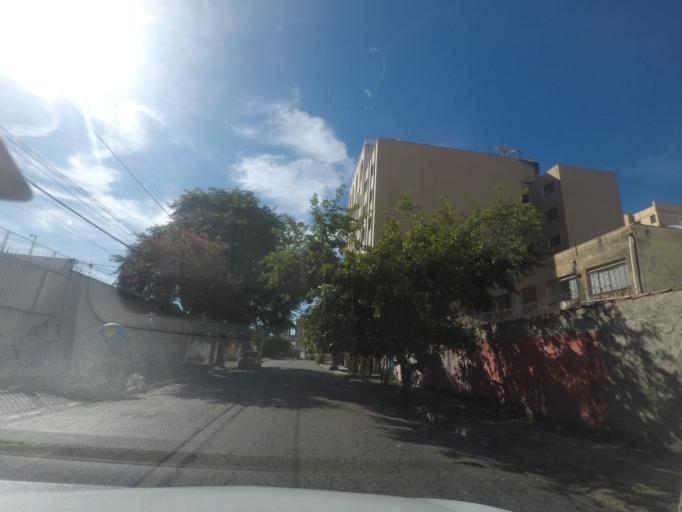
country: BR
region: Goias
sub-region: Goiania
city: Goiania
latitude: -16.6715
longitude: -49.2657
